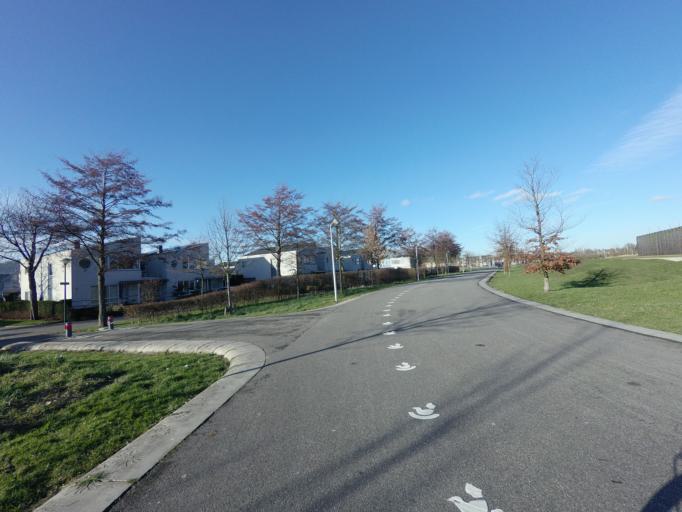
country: NL
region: Utrecht
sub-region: Stichtse Vecht
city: Maarssen
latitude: 52.0864
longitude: 5.0405
